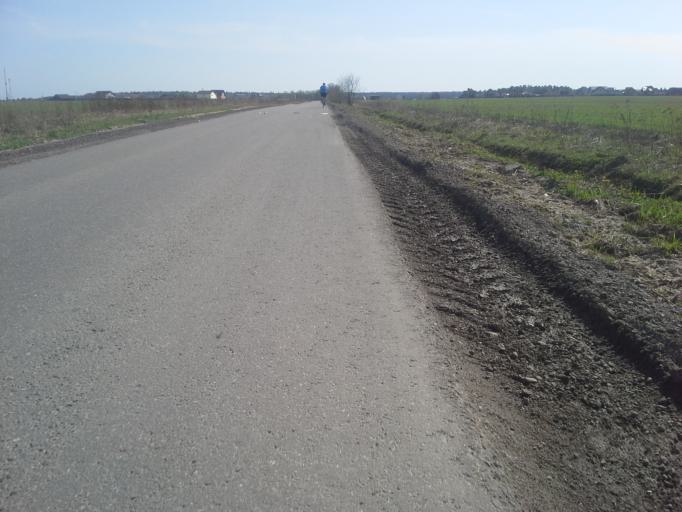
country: RU
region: Moskovskaya
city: Dubrovitsy
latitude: 55.4604
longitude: 37.4433
